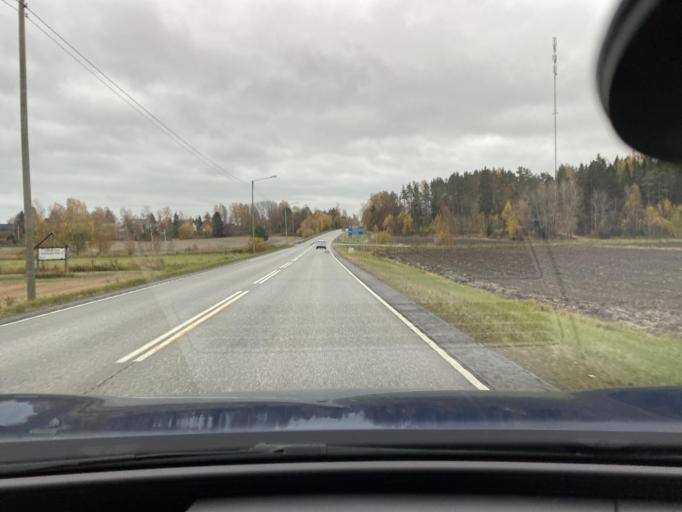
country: FI
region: Varsinais-Suomi
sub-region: Vakka-Suomi
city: Pyhaeranta
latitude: 60.9891
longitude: 21.5838
